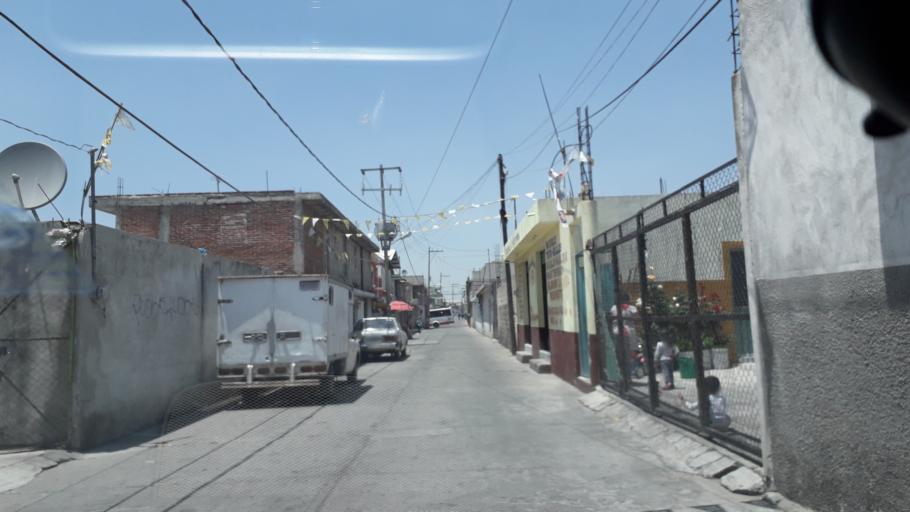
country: MX
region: Puebla
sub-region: Puebla
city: Santa Maria Xonacatepec
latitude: 19.0866
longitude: -98.1032
